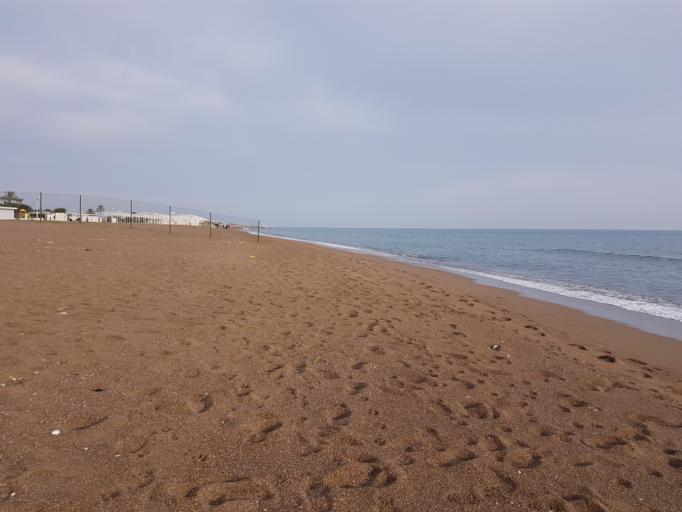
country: TR
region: Antalya
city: Aksu
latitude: 36.8481
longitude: 30.8267
